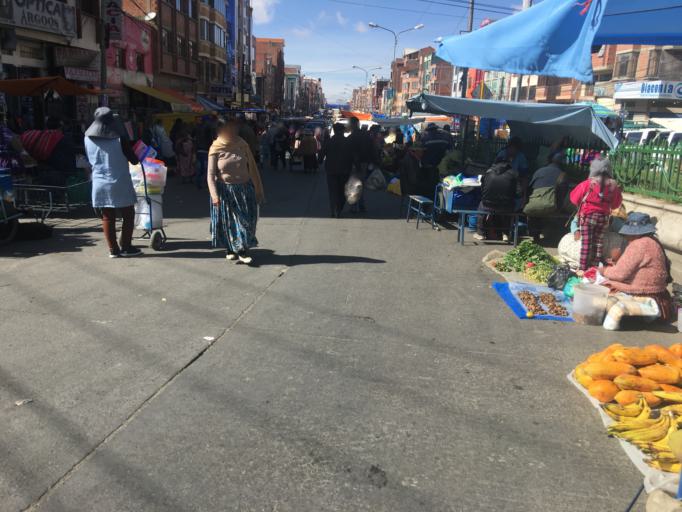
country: BO
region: La Paz
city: La Paz
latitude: -16.4888
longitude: -68.1718
